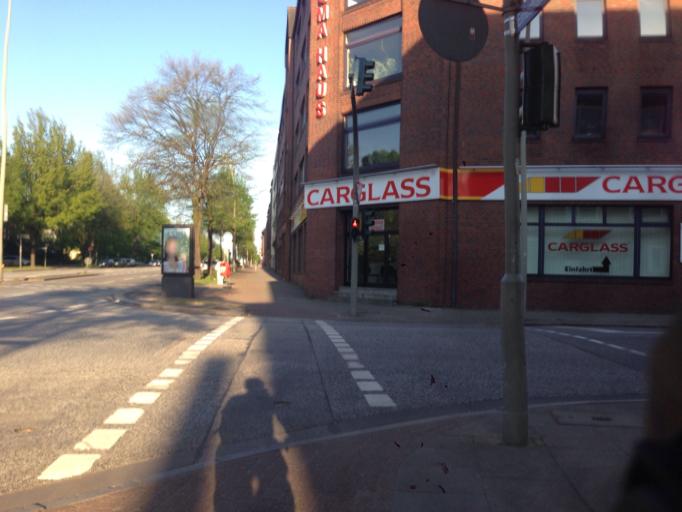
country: DE
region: Hamburg
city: Borgfelde
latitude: 53.5514
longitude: 10.0536
